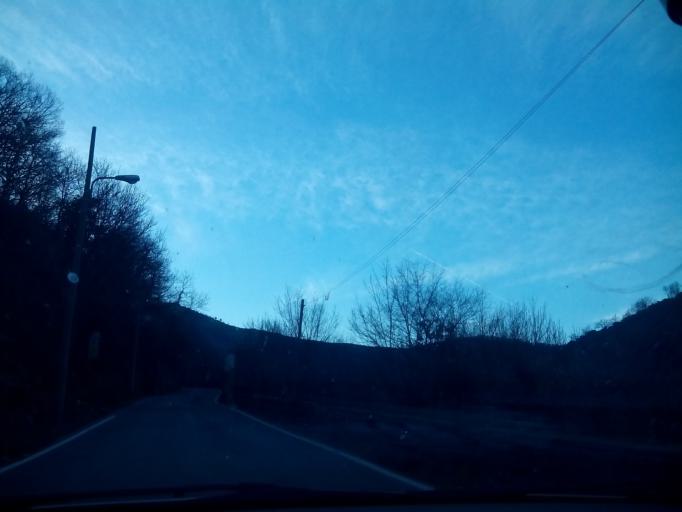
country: IT
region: Liguria
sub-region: Provincia di Genova
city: Piccarello
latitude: 44.4243
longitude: 9.0014
